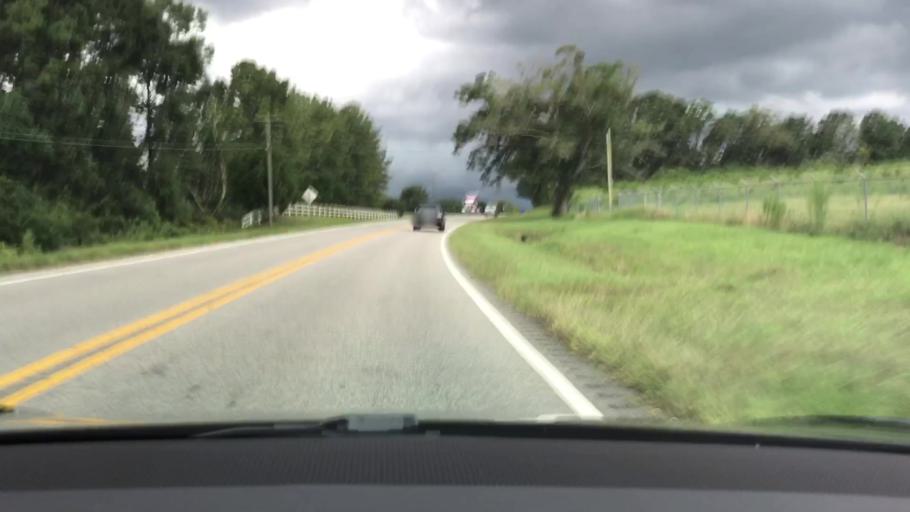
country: US
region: Alabama
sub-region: Coffee County
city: Elba
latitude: 31.4858
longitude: -86.0539
